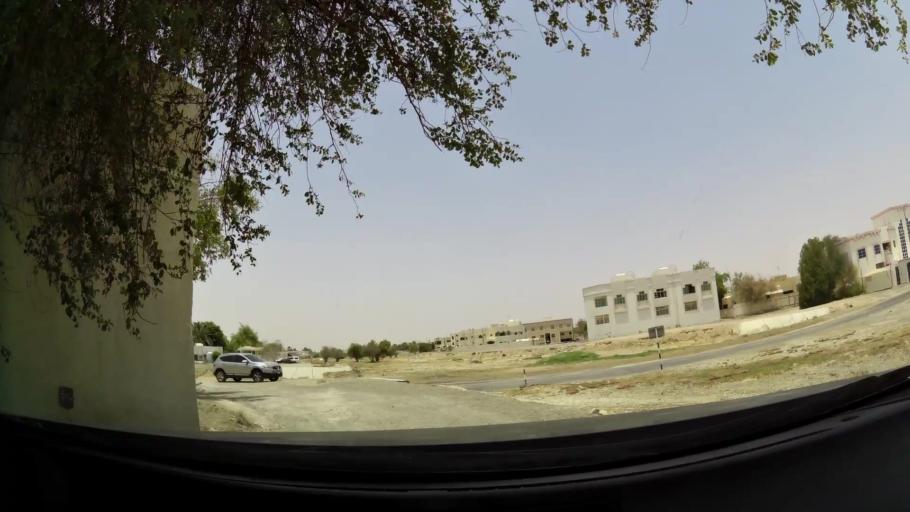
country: AE
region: Abu Dhabi
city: Al Ain
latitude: 24.2090
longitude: 55.7551
